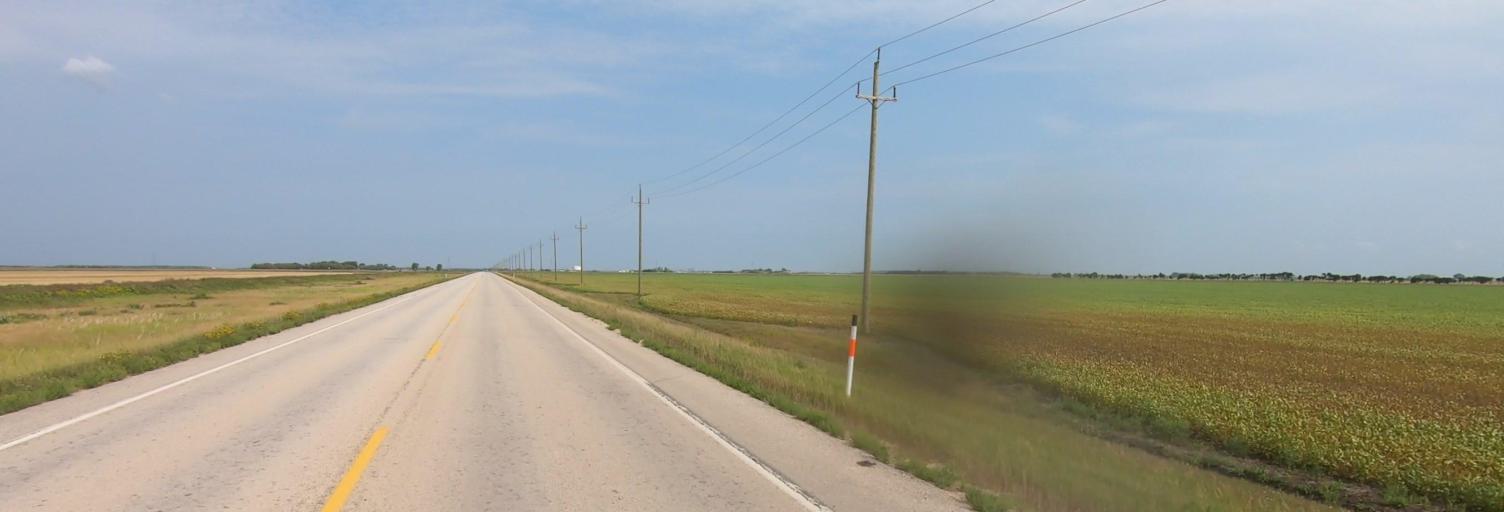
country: CA
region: Manitoba
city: Winnipeg
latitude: 49.7179
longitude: -97.2549
